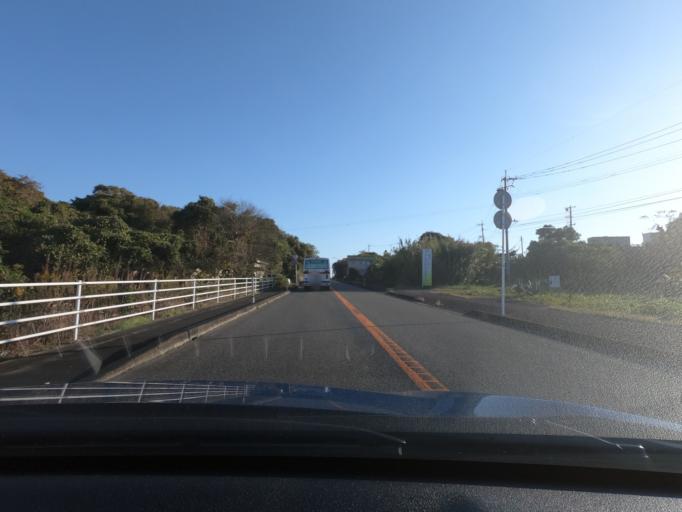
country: JP
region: Kagoshima
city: Akune
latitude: 31.9791
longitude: 130.2037
